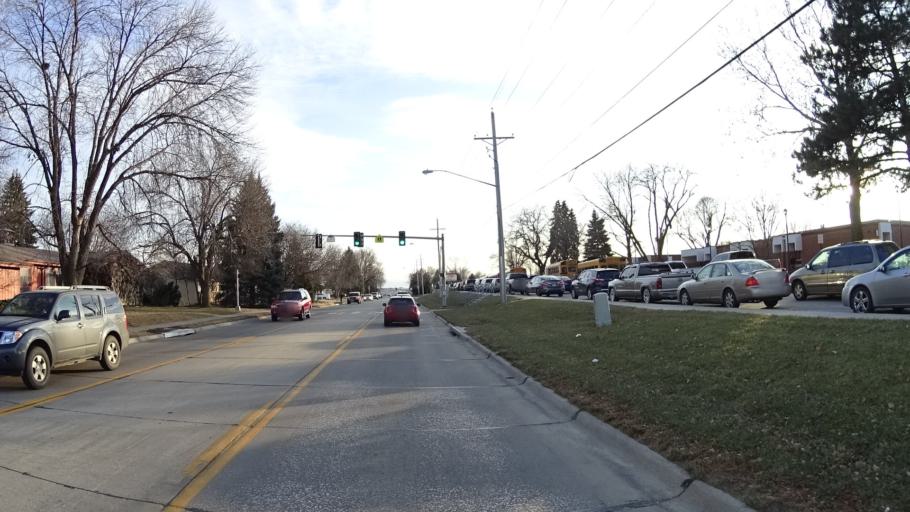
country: US
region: Nebraska
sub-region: Sarpy County
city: La Vista
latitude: 41.1867
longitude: -95.9867
